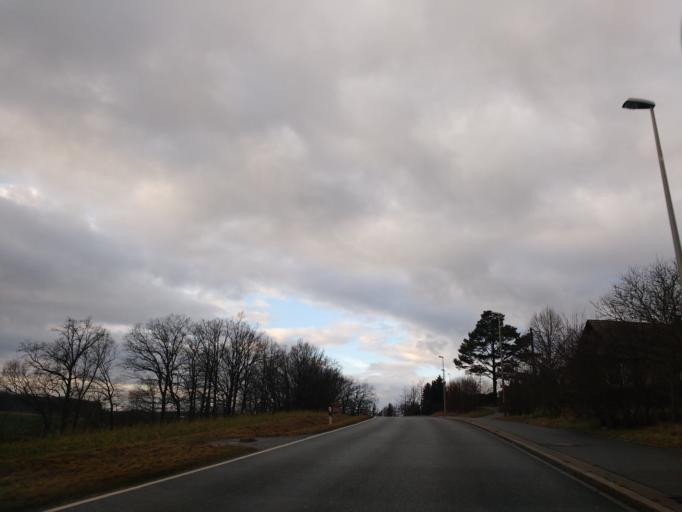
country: DE
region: Bavaria
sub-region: Regierungsbezirk Mittelfranken
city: Herzogenaurach
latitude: 49.5872
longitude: 10.8572
